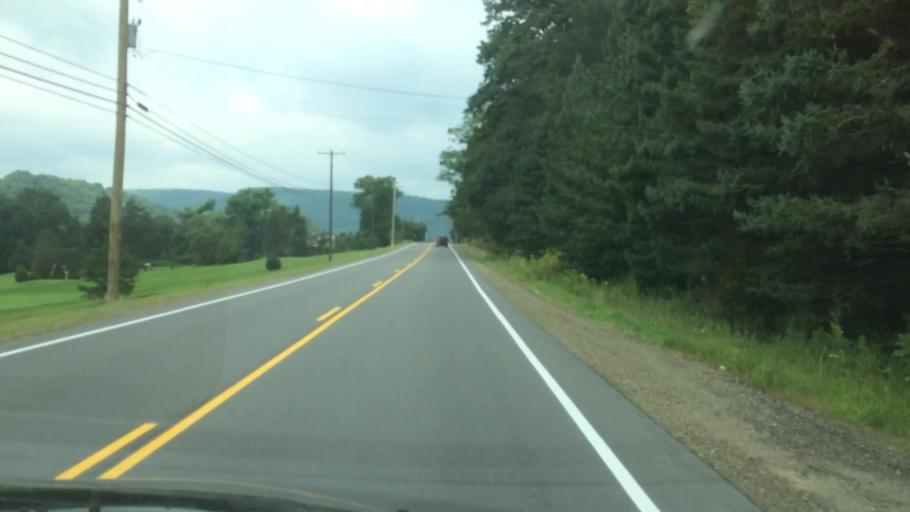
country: US
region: Pennsylvania
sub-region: McKean County
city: Bradford
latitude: 41.9066
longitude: -78.6214
